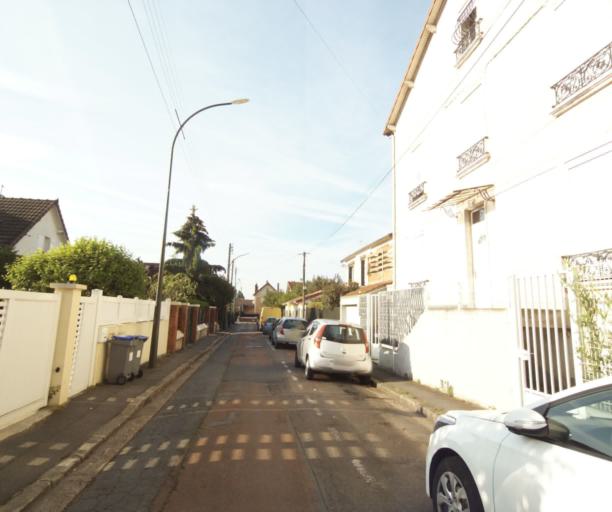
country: FR
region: Ile-de-France
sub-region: Departement du Val-d'Oise
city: Argenteuil
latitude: 48.9493
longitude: 2.2618
